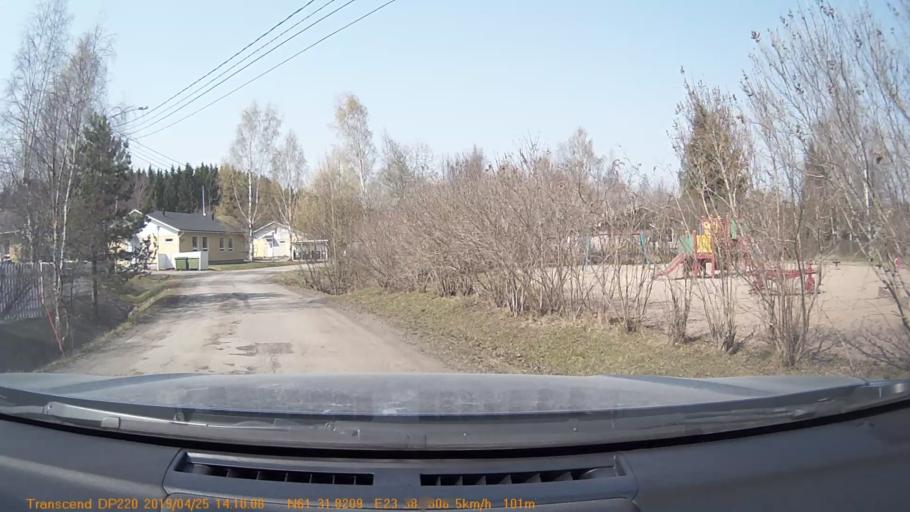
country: FI
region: Pirkanmaa
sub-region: Tampere
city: Yloejaervi
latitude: 61.5303
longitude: 23.6463
